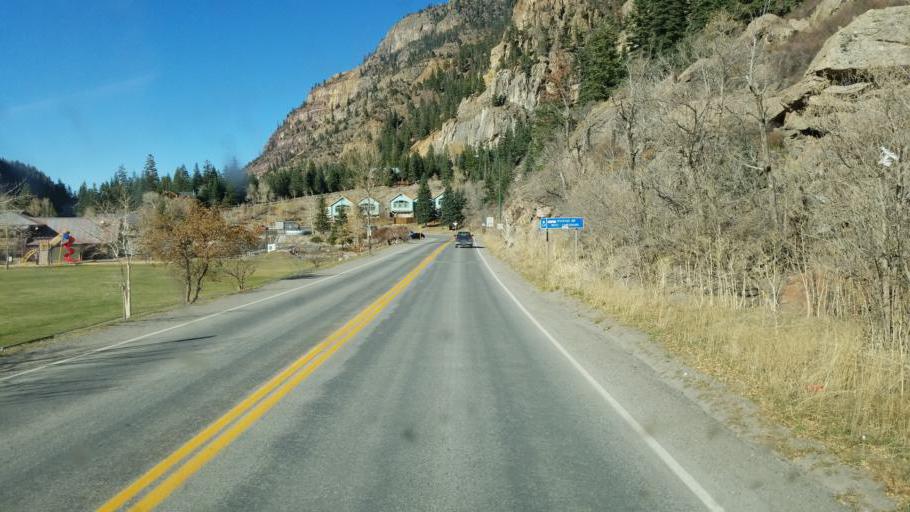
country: US
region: Colorado
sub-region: Ouray County
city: Ouray
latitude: 38.0277
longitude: -107.6714
